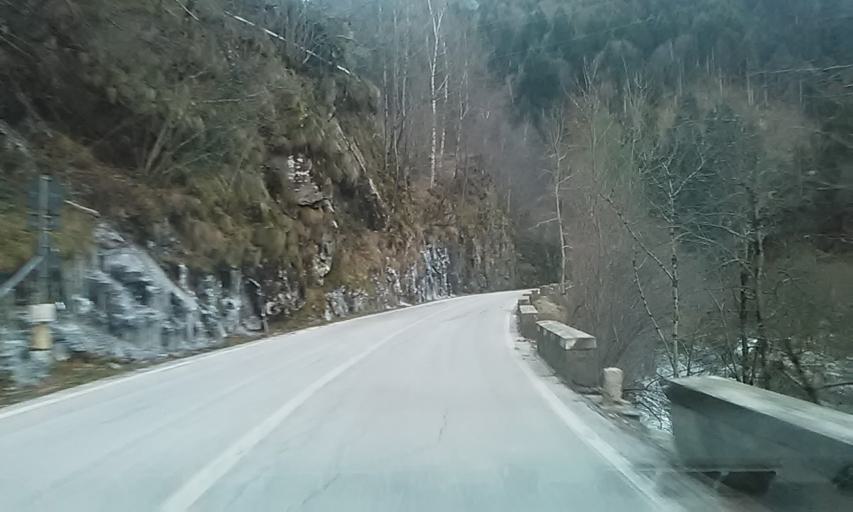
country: IT
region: Piedmont
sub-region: Provincia di Vercelli
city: Rimasco
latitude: 45.8432
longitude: 8.0714
